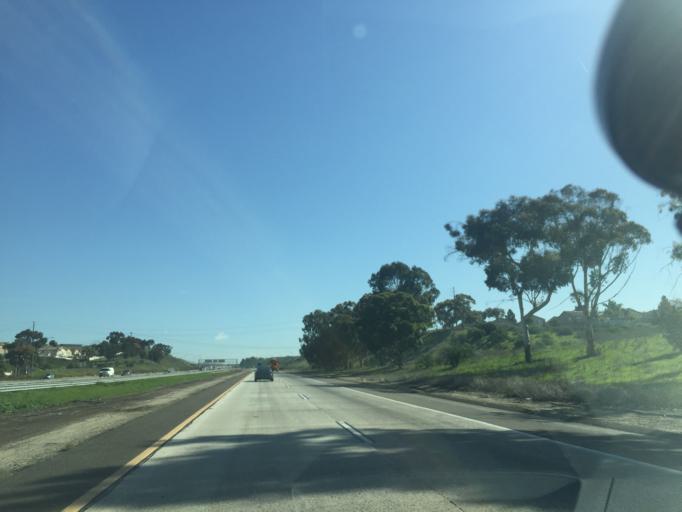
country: MX
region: Baja California
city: Tijuana
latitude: 32.5680
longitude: -117.0376
